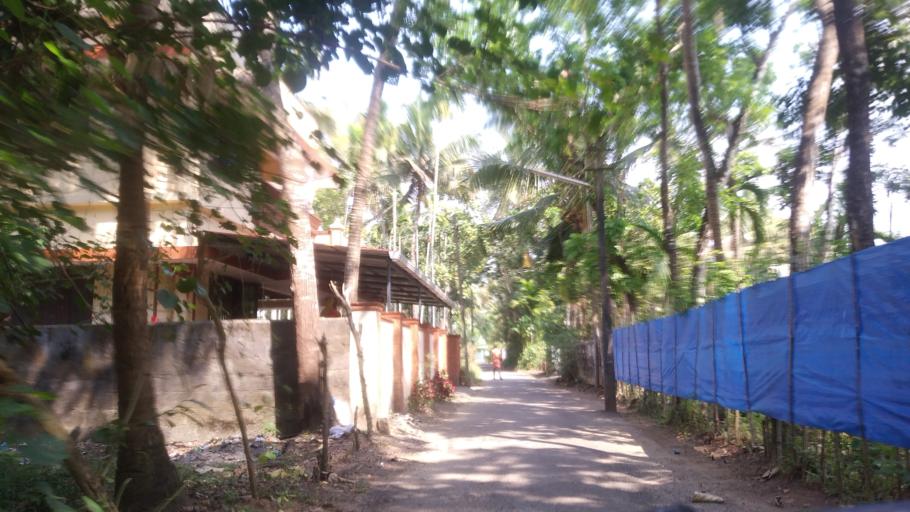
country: IN
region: Kerala
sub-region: Ernakulam
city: Elur
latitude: 10.1227
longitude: 76.2354
